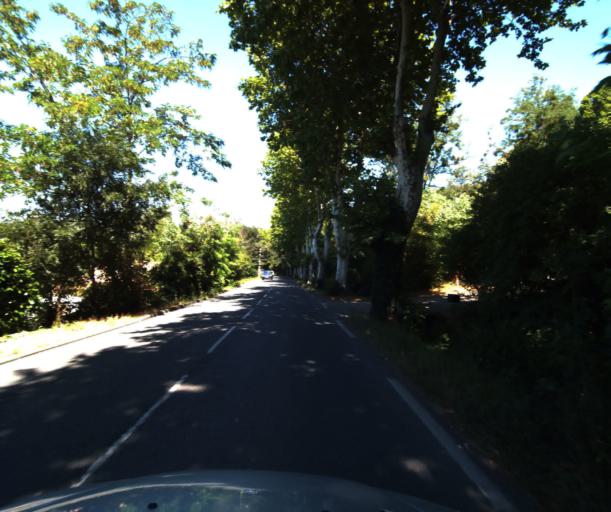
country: FR
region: Midi-Pyrenees
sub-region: Departement de la Haute-Garonne
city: Muret
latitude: 43.4511
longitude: 1.3331
